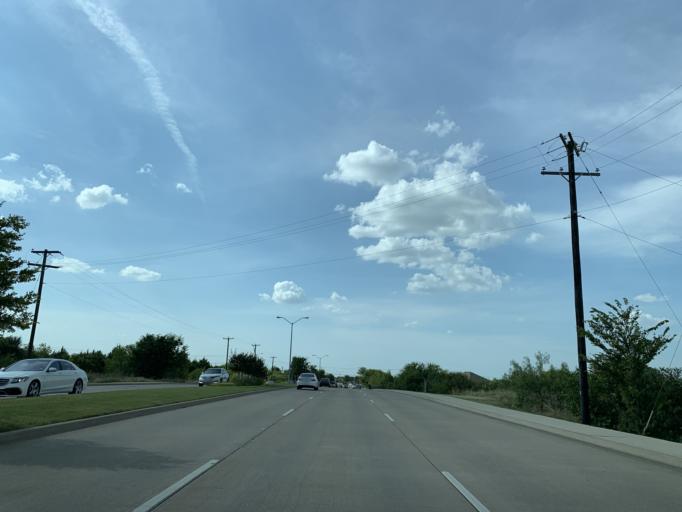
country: US
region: Texas
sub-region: Dallas County
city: Cedar Hill
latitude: 32.6375
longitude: -97.0462
